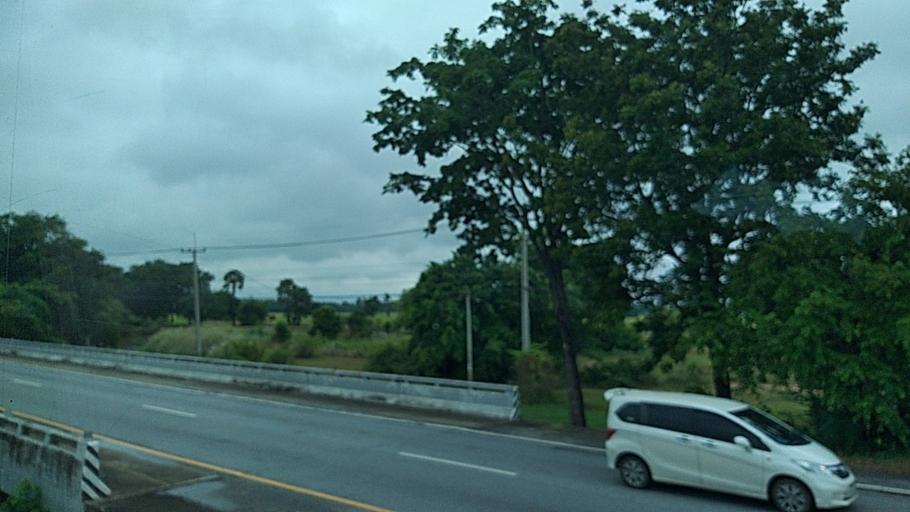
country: TH
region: Nakhon Ratchasima
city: Sida
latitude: 15.5189
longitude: 102.5400
